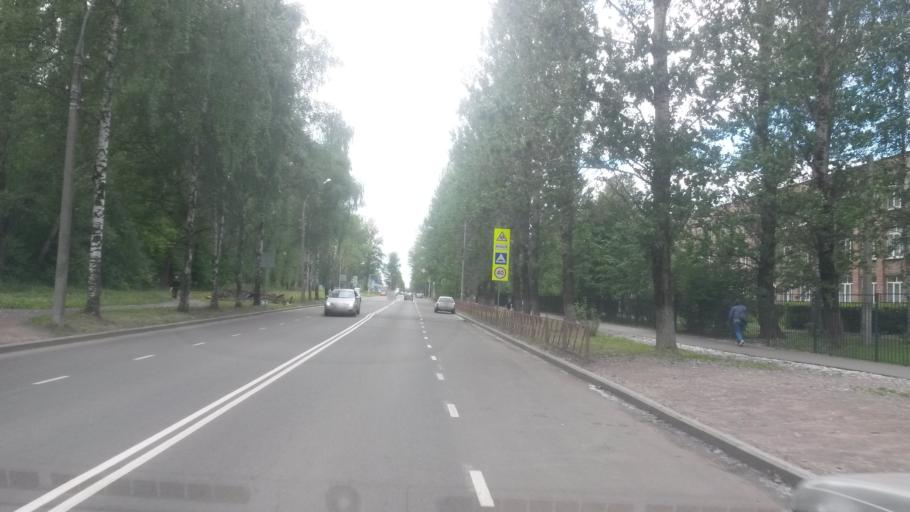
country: RU
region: Jaroslavl
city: Yaroslavl
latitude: 57.6807
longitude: 39.8042
